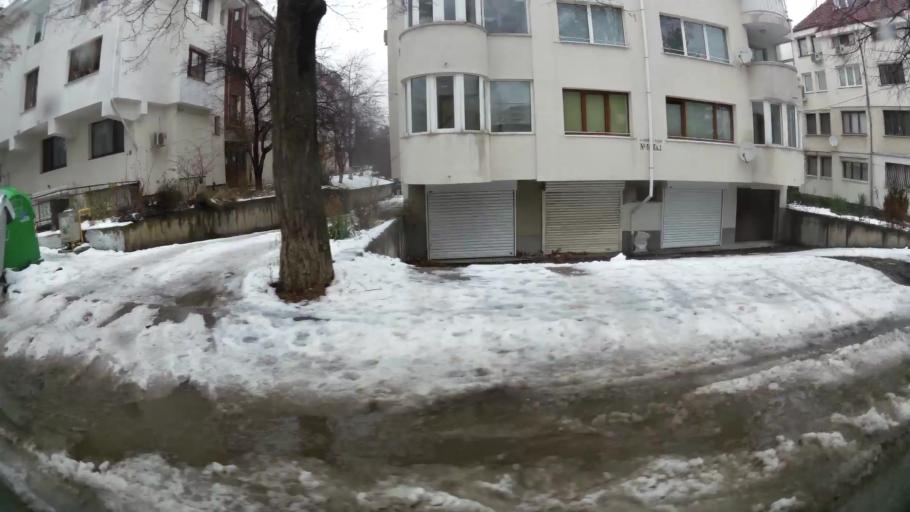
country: BG
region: Sofia-Capital
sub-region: Stolichna Obshtina
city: Sofia
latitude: 42.6628
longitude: 23.2703
